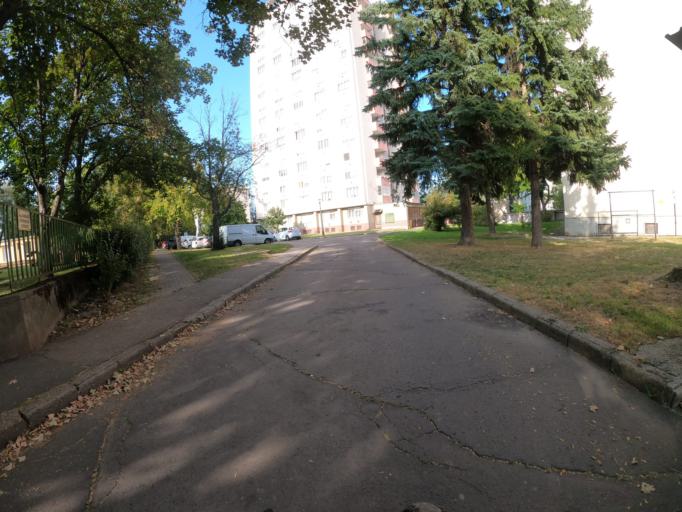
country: HU
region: Borsod-Abauj-Zemplen
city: Sajobabony
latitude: 48.0965
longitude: 20.7039
